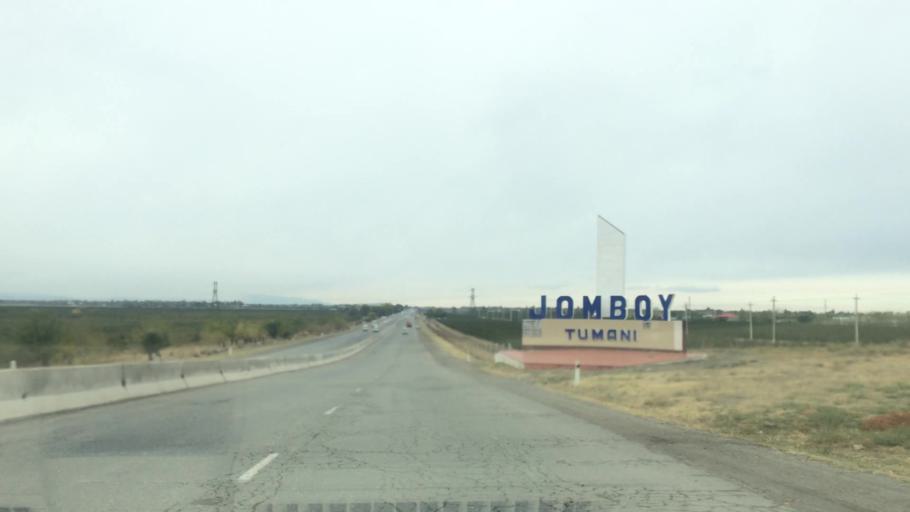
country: UZ
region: Samarqand
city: Bulung'ur
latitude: 39.7568
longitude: 67.2434
